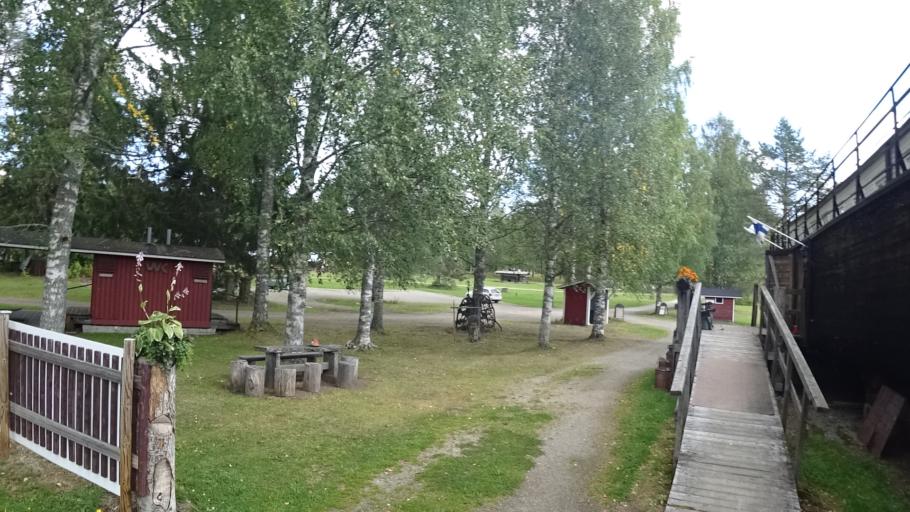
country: FI
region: North Karelia
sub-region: Joensuu
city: Ilomantsi
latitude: 62.6409
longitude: 31.2845
